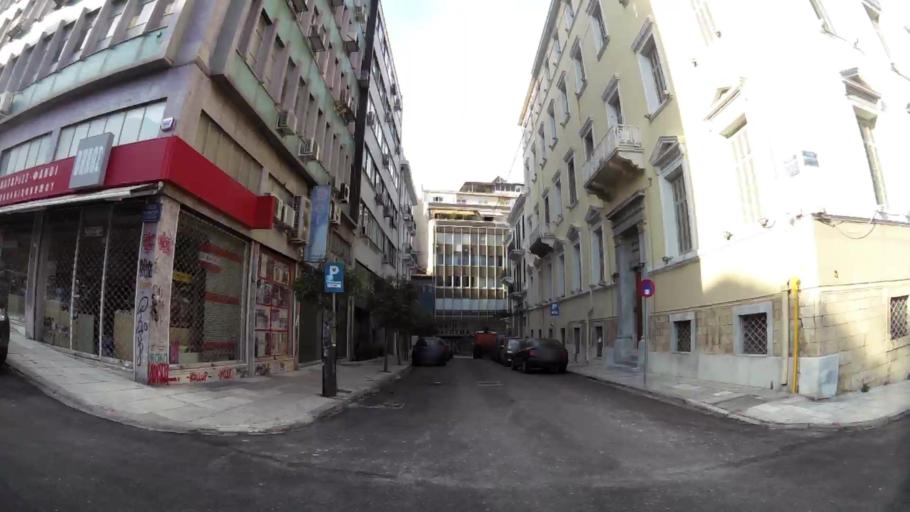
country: GR
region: Attica
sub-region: Nomarchia Athinas
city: Athens
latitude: 37.9787
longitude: 23.7308
